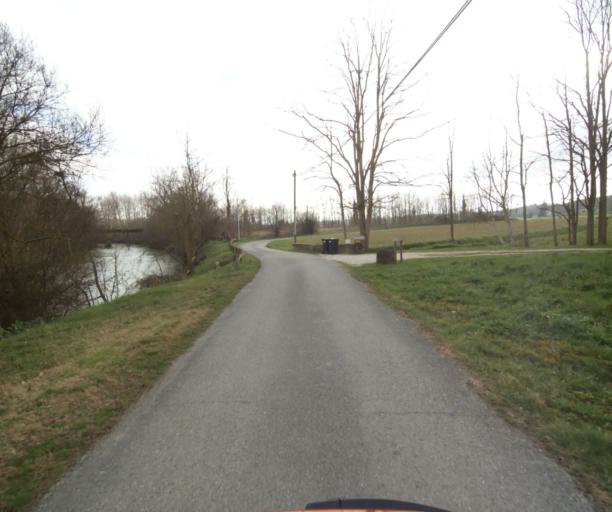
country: FR
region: Languedoc-Roussillon
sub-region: Departement de l'Aude
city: Belpech
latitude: 43.1739
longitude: 1.7303
